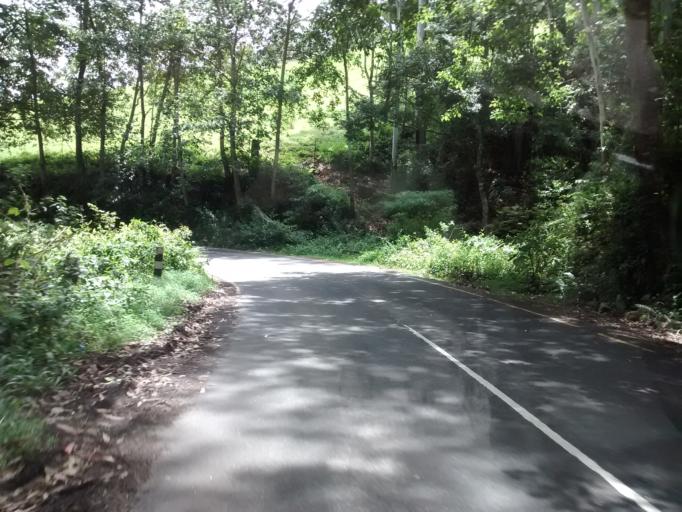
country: IN
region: Kerala
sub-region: Idukki
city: Munnar
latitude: 10.1175
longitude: 77.1404
